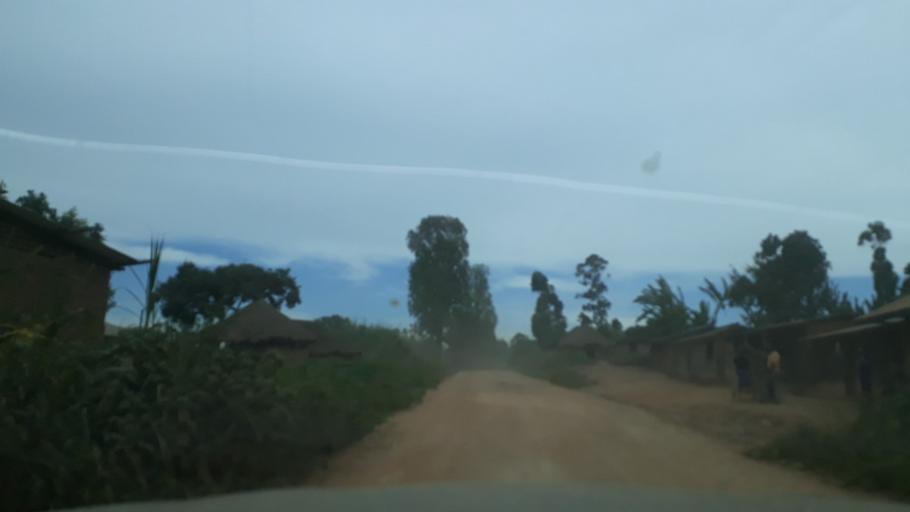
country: CD
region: Eastern Province
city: Bunia
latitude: 1.8960
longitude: 30.4905
